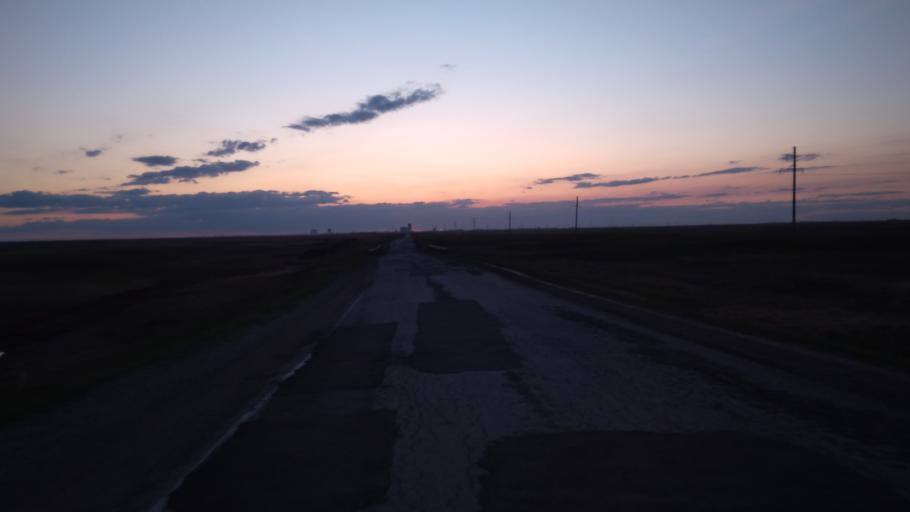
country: RU
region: Chelyabinsk
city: Troitsk
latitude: 54.0877
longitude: 61.6556
